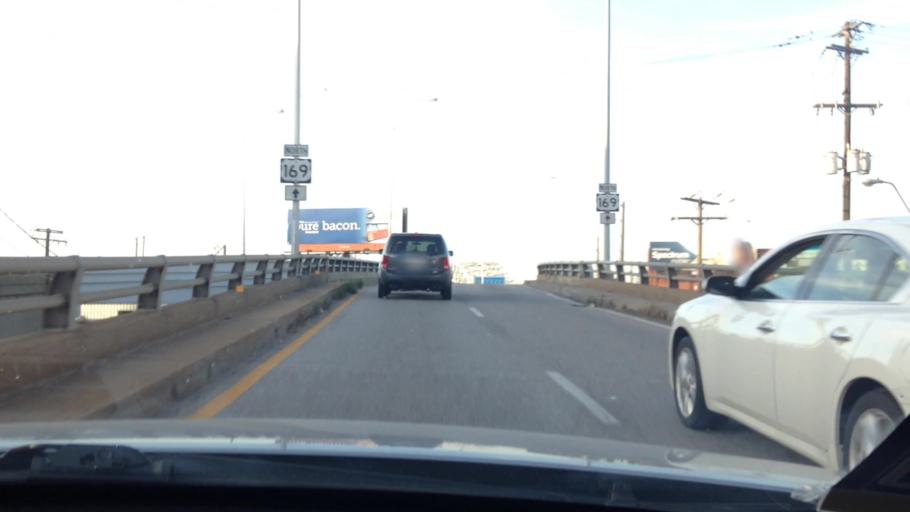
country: US
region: Missouri
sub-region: Jackson County
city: Kansas City
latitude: 39.1078
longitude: -94.5883
